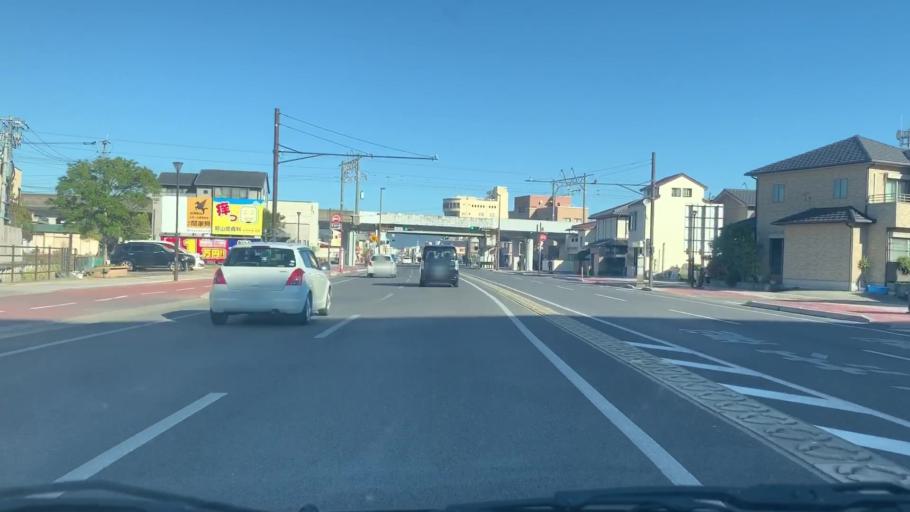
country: JP
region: Saga Prefecture
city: Saga-shi
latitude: 33.2624
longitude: 130.2933
